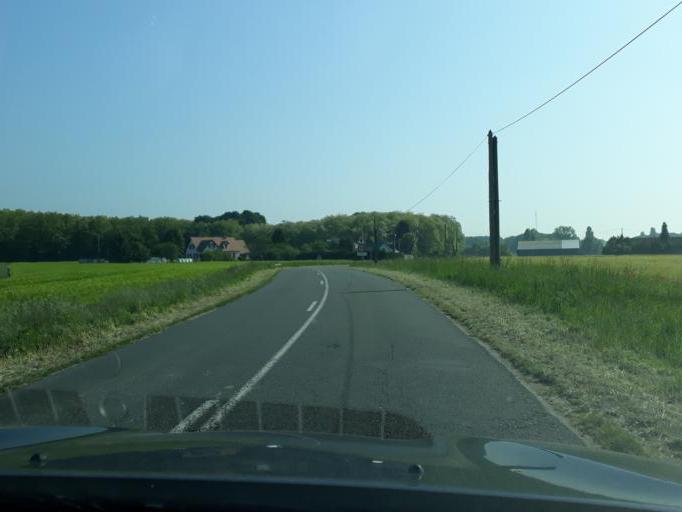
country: FR
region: Centre
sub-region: Departement du Loiret
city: Vennecy
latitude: 47.9513
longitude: 2.0724
